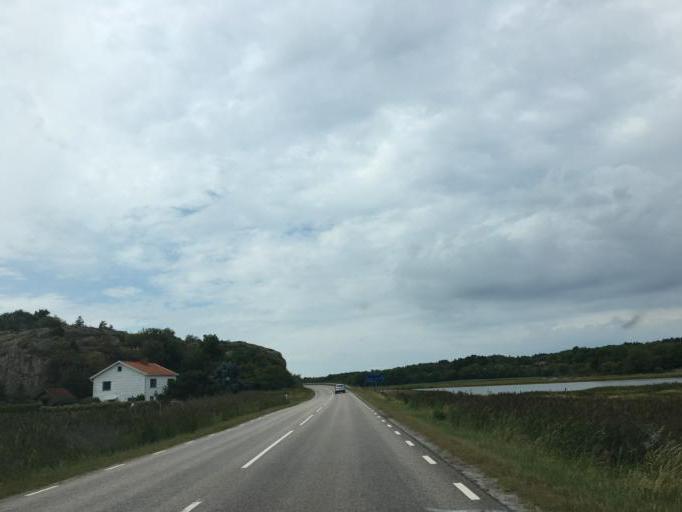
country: SE
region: Vaestra Goetaland
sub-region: Sotenas Kommun
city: Hunnebostrand
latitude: 58.4253
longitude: 11.2946
